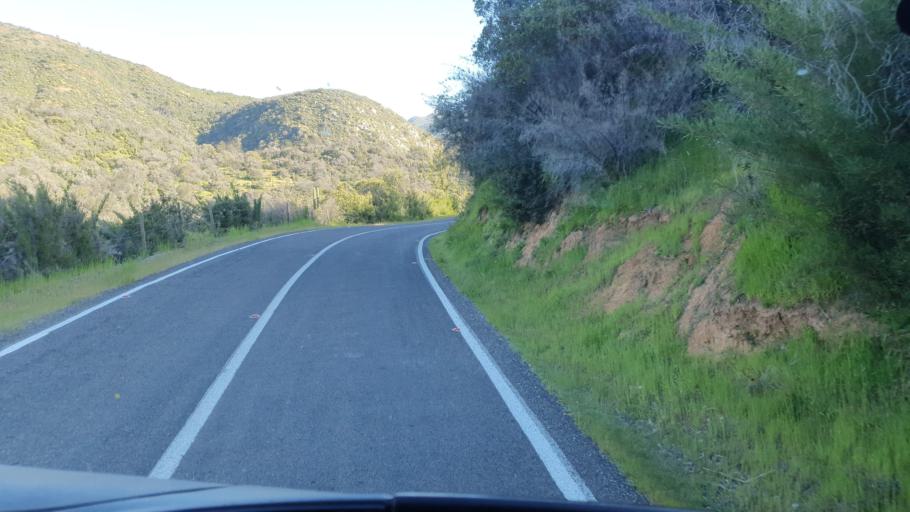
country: CL
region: Valparaiso
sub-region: Provincia de Marga Marga
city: Limache
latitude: -33.1827
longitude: -71.1735
